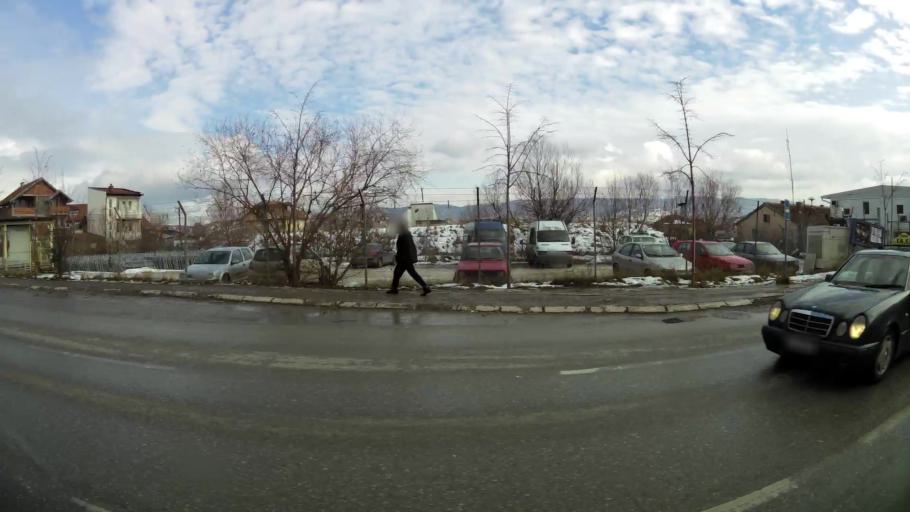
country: XK
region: Pristina
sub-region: Komuna e Prishtines
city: Pristina
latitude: 42.6817
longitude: 21.1594
